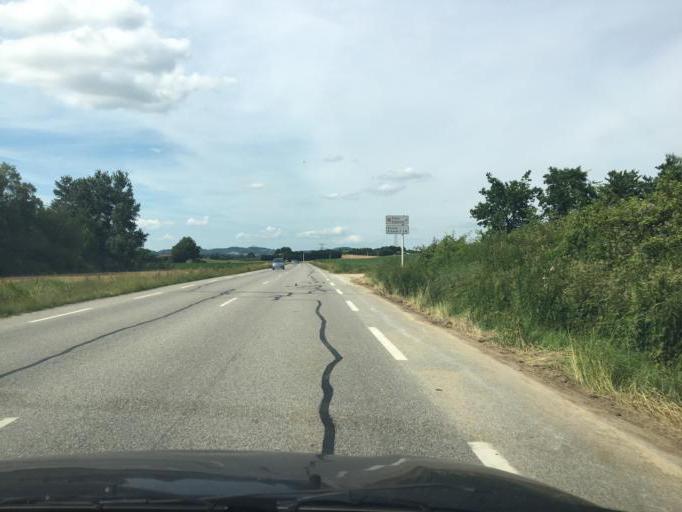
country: FR
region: Rhone-Alpes
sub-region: Departement de la Drome
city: Chanos-Curson
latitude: 45.0762
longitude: 4.9362
